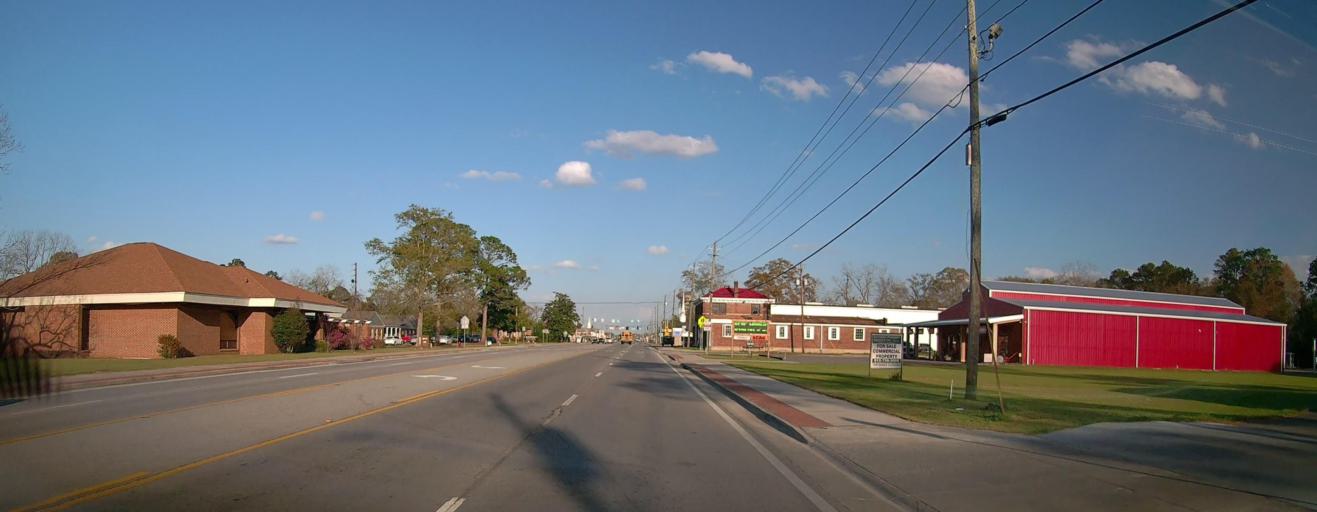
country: US
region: Georgia
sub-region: Evans County
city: Claxton
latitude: 32.1610
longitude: -81.9168
